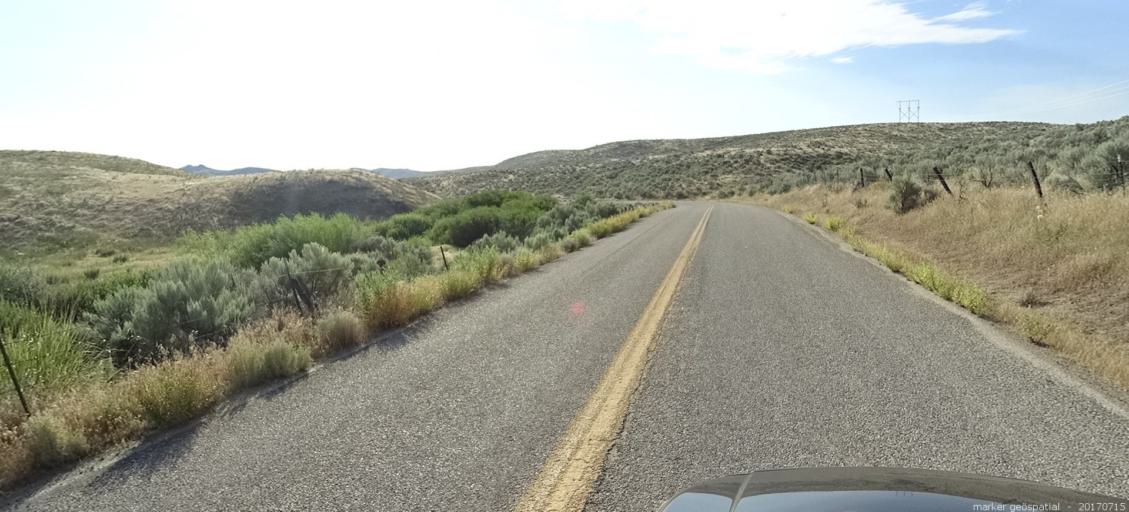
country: US
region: Idaho
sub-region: Ada County
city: Boise
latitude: 43.4804
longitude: -115.9822
